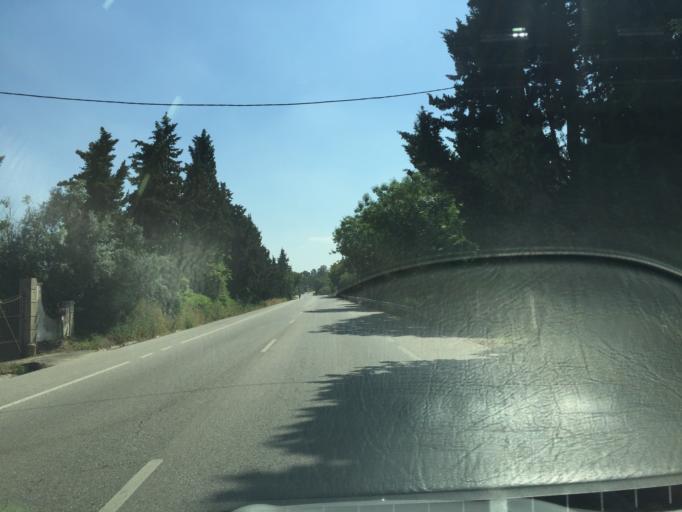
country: PT
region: Santarem
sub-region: Golega
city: Golega
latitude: 39.3837
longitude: -8.4514
